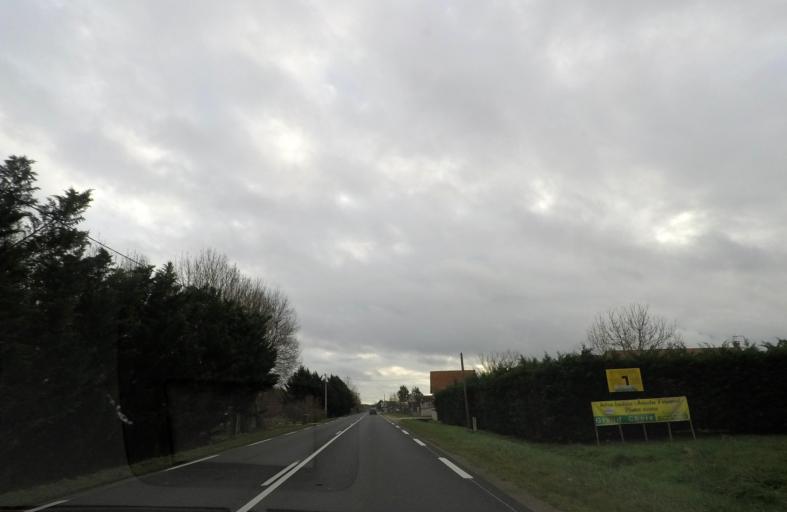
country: FR
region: Centre
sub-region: Departement du Loir-et-Cher
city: Soings-en-Sologne
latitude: 47.4639
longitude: 1.5164
